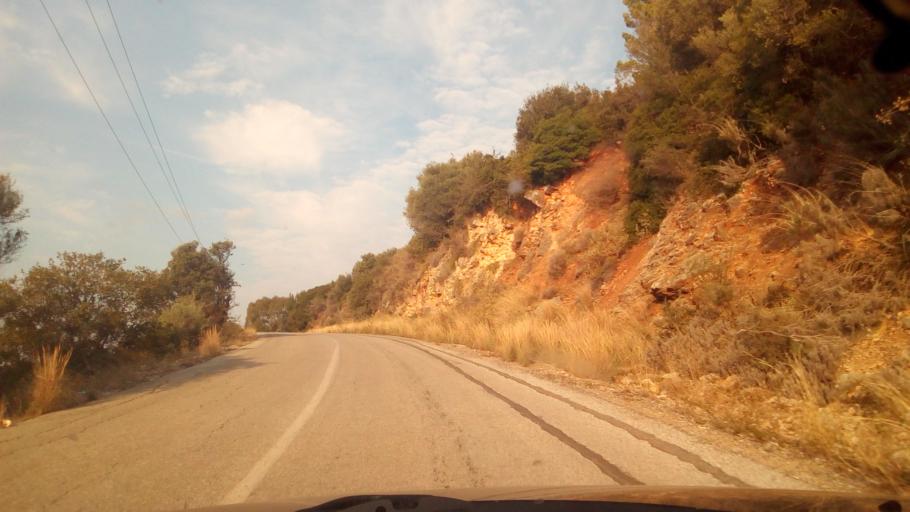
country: GR
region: West Greece
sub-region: Nomos Aitolias kai Akarnanias
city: Nafpaktos
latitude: 38.4086
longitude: 21.9351
